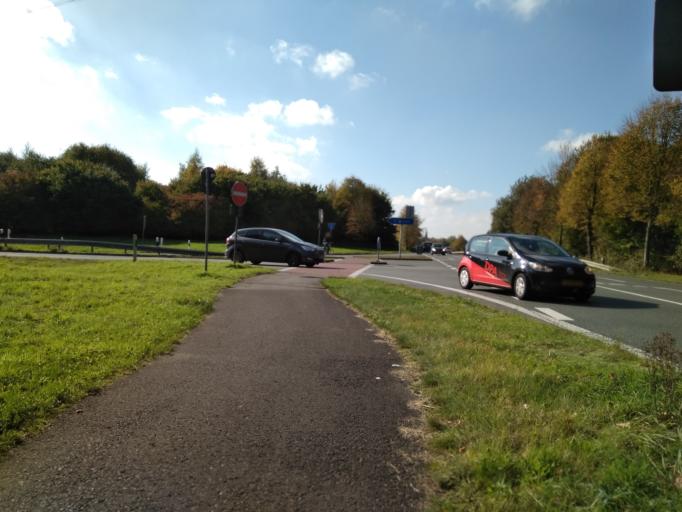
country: DE
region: North Rhine-Westphalia
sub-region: Regierungsbezirk Munster
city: Gladbeck
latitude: 51.6082
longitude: 6.9425
